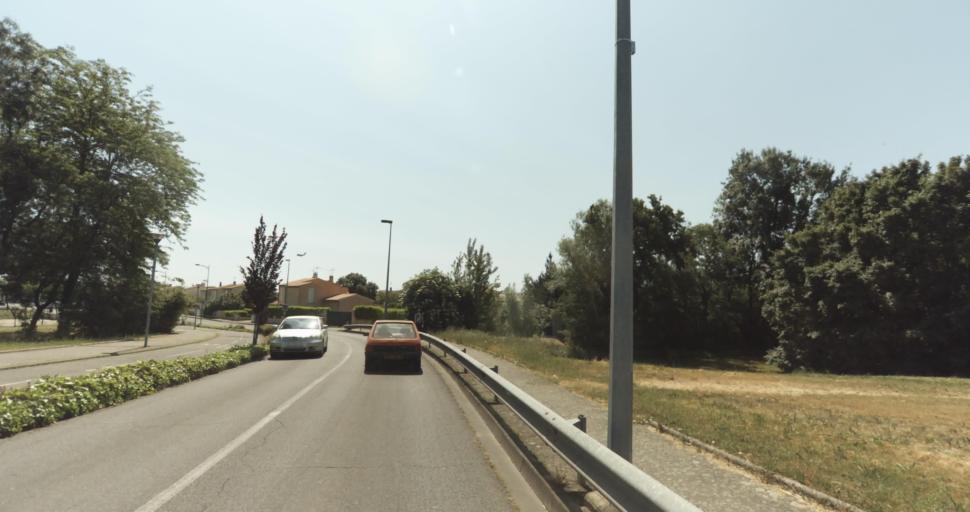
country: FR
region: Midi-Pyrenees
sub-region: Departement de la Haute-Garonne
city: Plaisance-du-Touch
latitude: 43.5630
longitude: 1.3003
